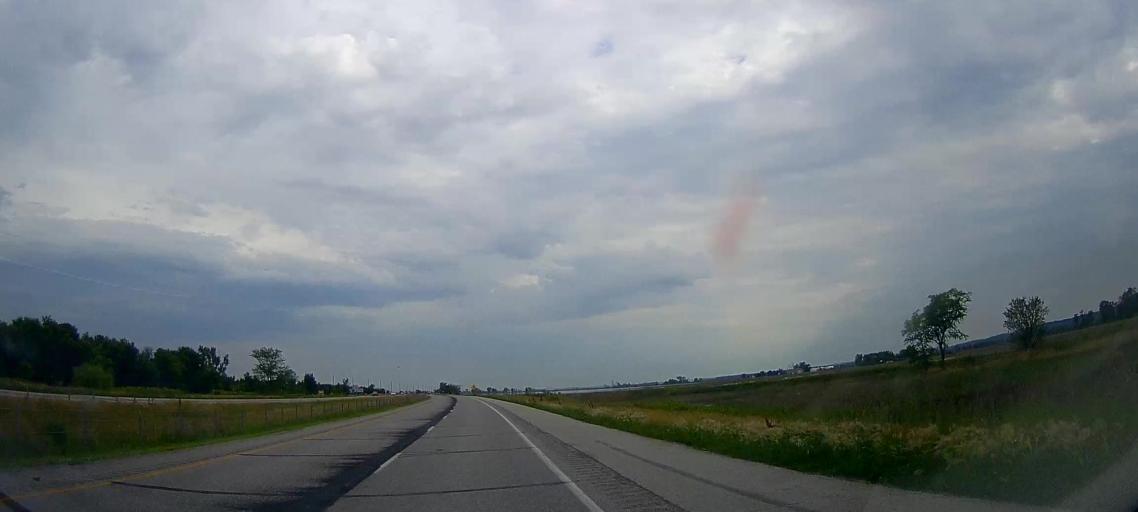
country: US
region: Iowa
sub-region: Pottawattamie County
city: Carter Lake
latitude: 41.4185
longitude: -95.9009
